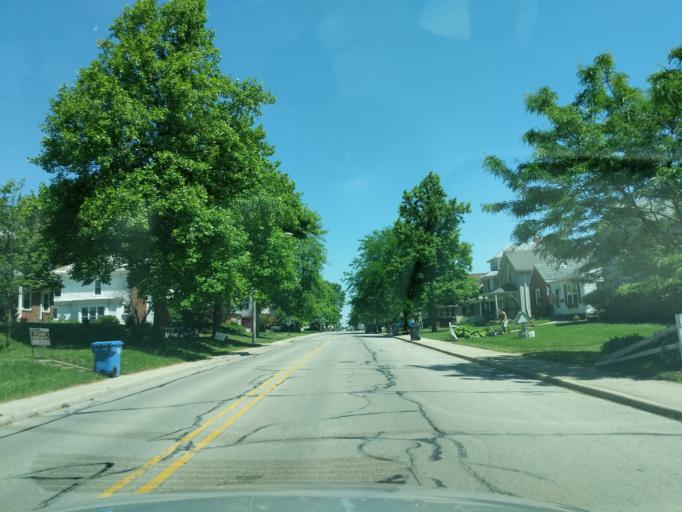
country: US
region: Indiana
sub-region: Whitley County
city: Columbia City
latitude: 41.1601
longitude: -85.4914
